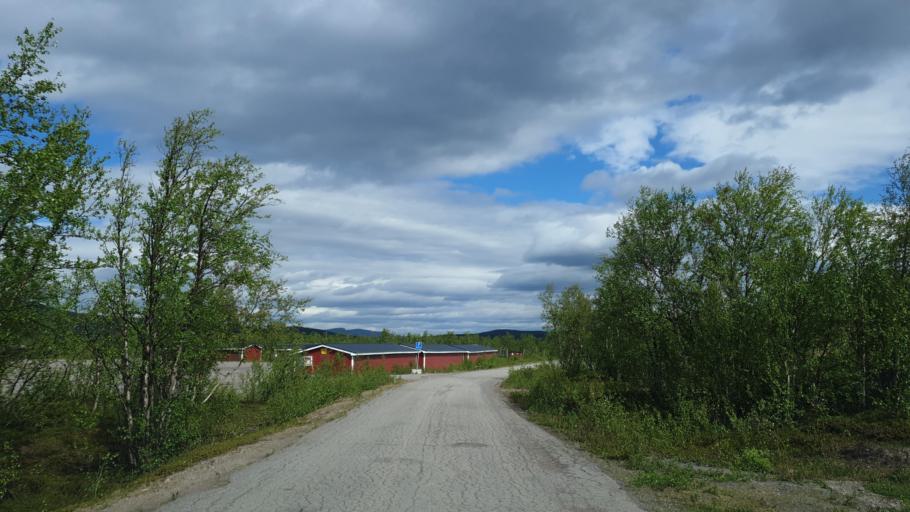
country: SE
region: Norrbotten
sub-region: Kiruna Kommun
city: Kiruna
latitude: 68.2253
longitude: 19.7180
